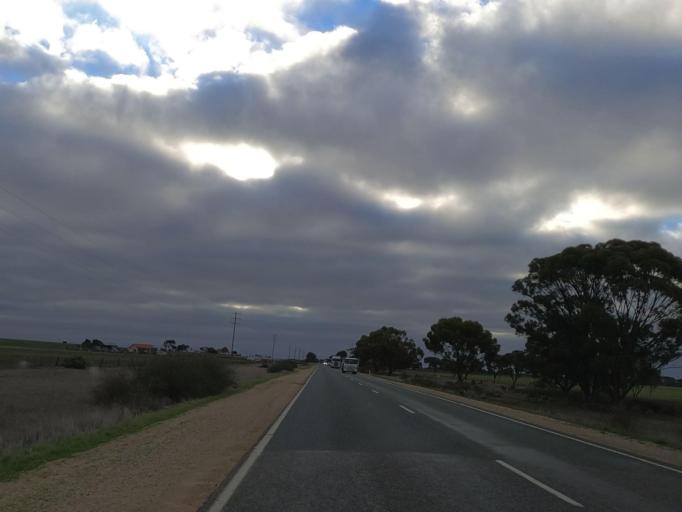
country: AU
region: Victoria
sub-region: Swan Hill
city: Swan Hill
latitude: -35.6452
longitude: 143.8337
